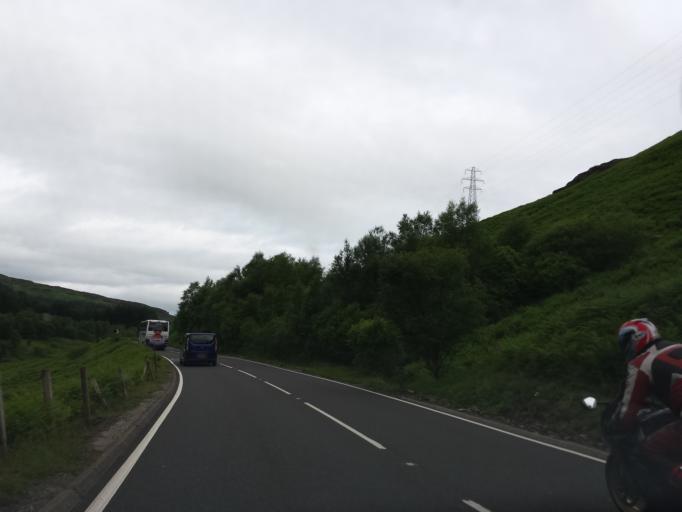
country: GB
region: Scotland
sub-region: Stirling
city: Callander
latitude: 56.4142
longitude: -4.3237
